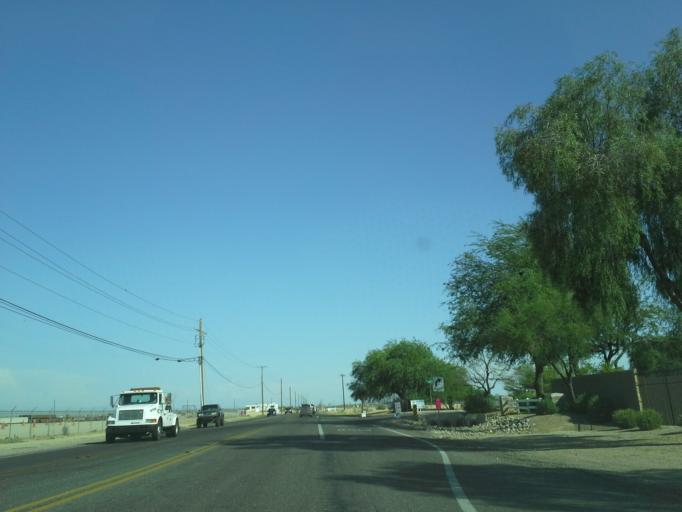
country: US
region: Arizona
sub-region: Pinal County
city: San Tan Valley
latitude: 33.1538
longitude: -111.5565
